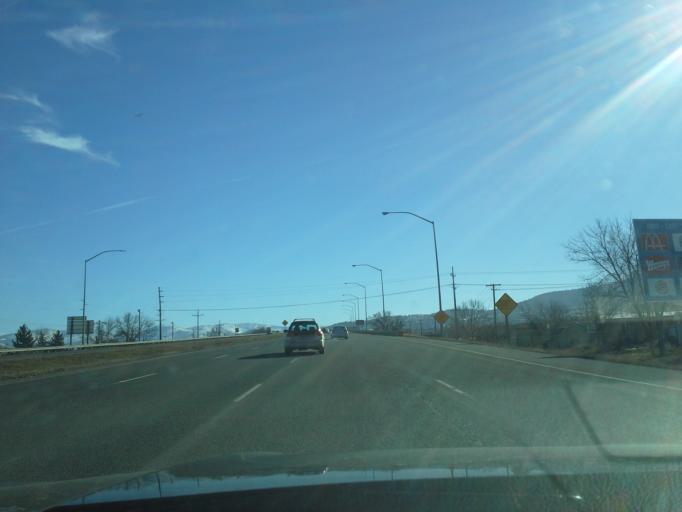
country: US
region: Montana
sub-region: Lewis and Clark County
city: Helena
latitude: 46.6036
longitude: -112.0064
